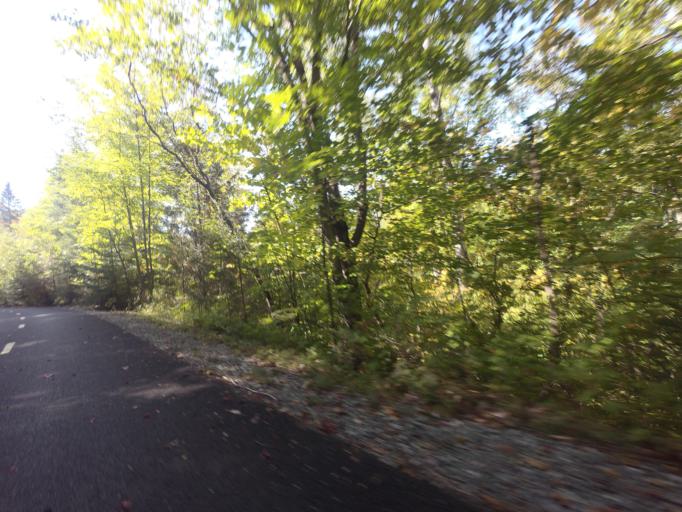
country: CA
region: Quebec
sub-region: Laurentides
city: Mont-Tremblant
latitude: 46.1222
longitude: -74.5004
